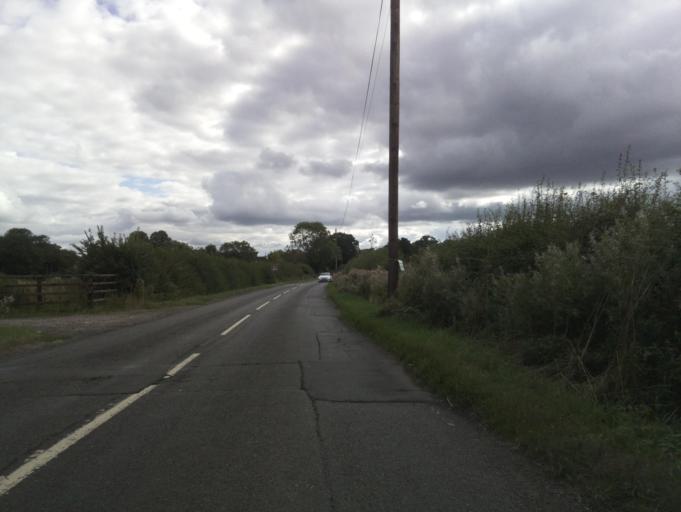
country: GB
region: England
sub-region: Leicestershire
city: Loughborough
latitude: 52.7969
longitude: -1.1976
